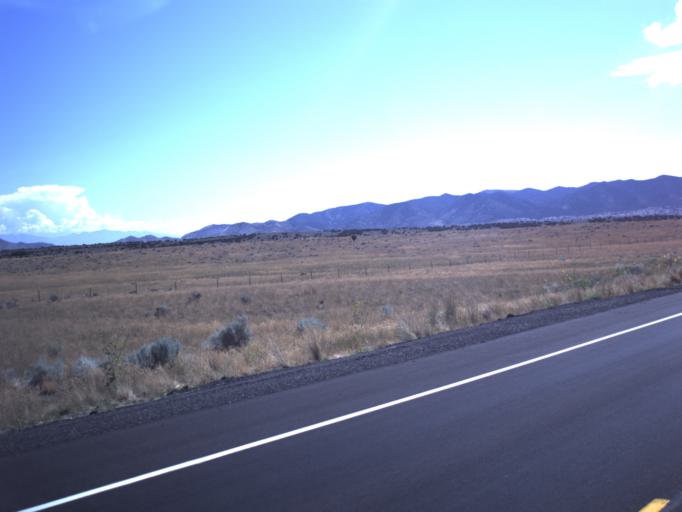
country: US
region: Utah
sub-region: Utah County
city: Eagle Mountain
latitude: 40.0620
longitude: -112.3152
